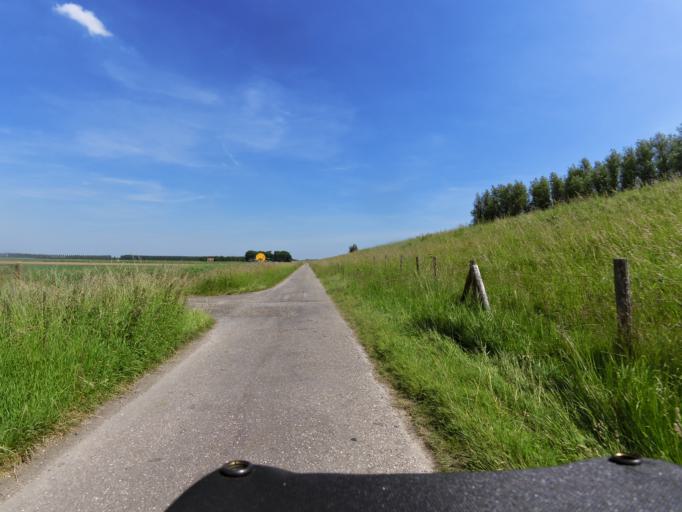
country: NL
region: South Holland
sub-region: Gemeente Spijkenisse
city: Spijkenisse
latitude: 51.7589
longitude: 4.2911
